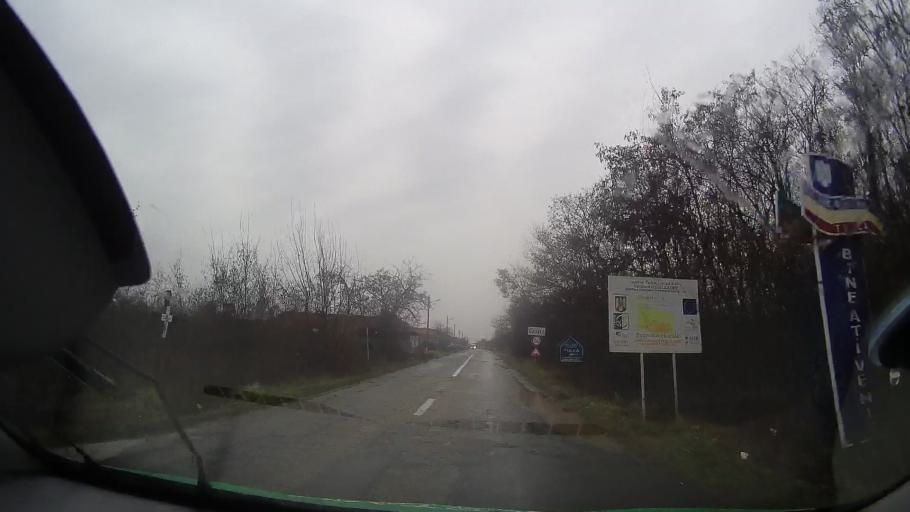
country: RO
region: Bihor
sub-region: Comuna Tinca
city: Gurbediu
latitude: 46.7900
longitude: 21.8294
